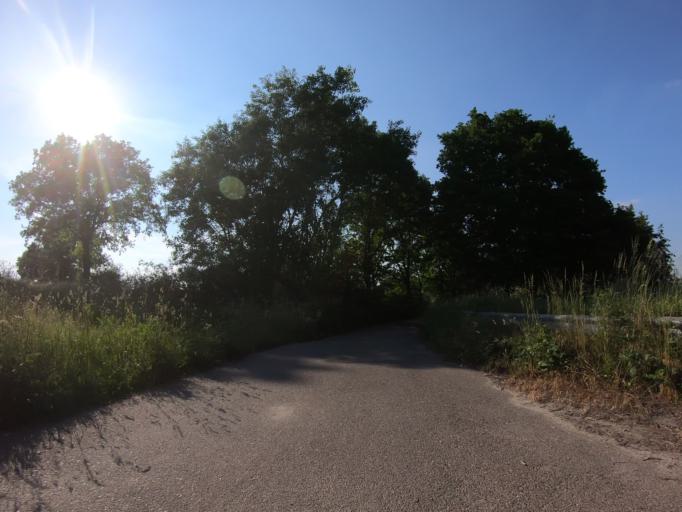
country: DE
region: Lower Saxony
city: Calberlah
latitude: 52.4097
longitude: 10.6158
